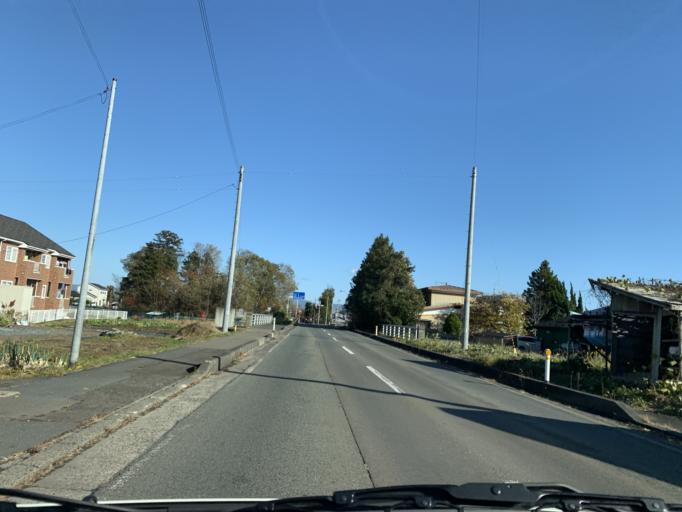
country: JP
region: Iwate
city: Mizusawa
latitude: 39.1643
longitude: 141.1306
